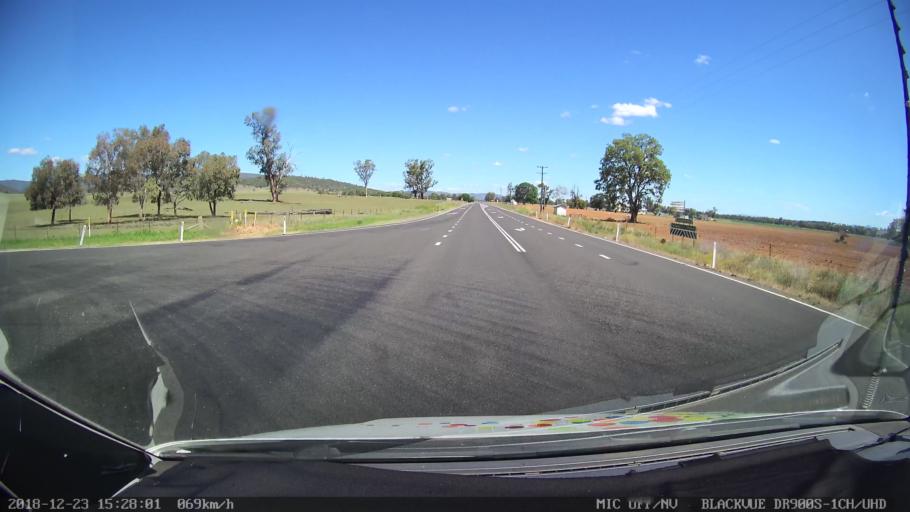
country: AU
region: New South Wales
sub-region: Tamworth Municipality
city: East Tamworth
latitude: -30.9324
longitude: 150.8492
